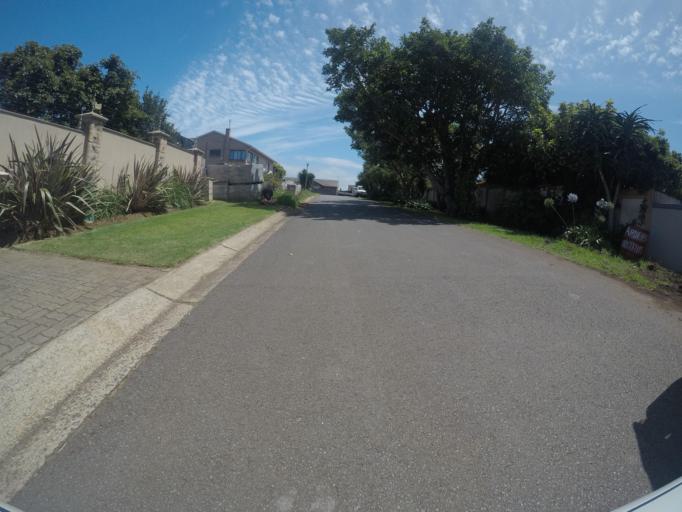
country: ZA
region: Eastern Cape
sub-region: Buffalo City Metropolitan Municipality
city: East London
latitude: -32.9410
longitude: 27.9973
